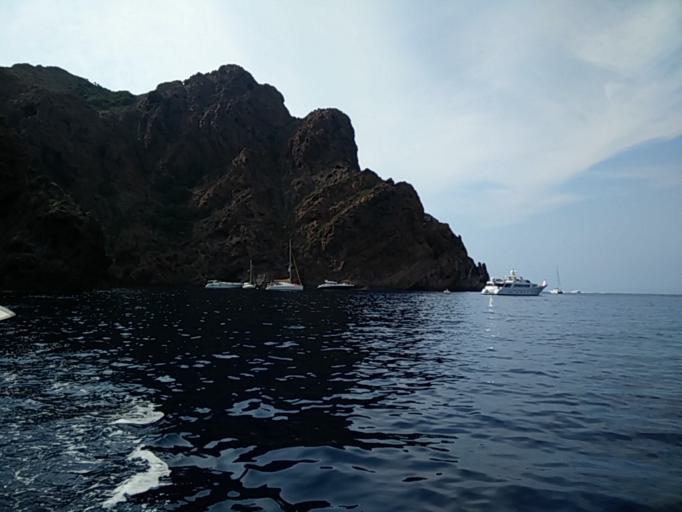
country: FR
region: Corsica
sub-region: Departement de la Corse-du-Sud
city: Cargese
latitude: 42.3724
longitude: 8.5544
